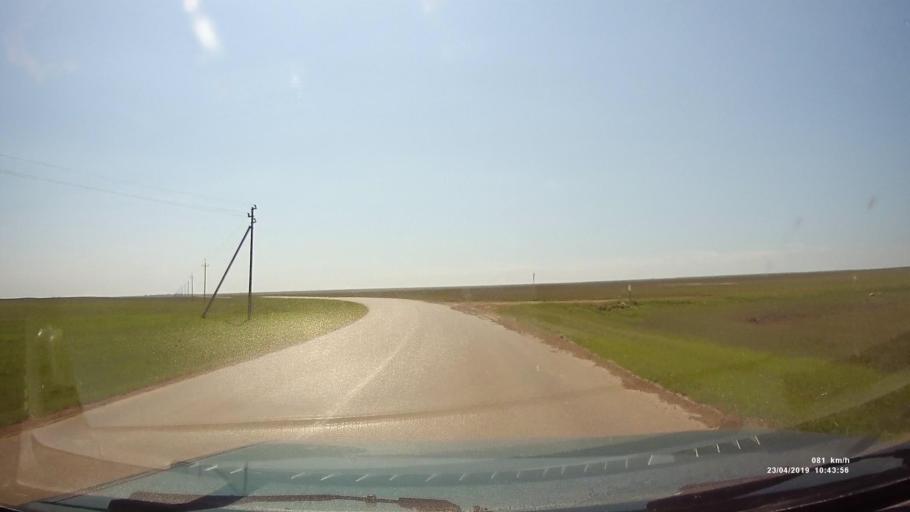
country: RU
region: Kalmykiya
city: Yashalta
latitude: 46.4640
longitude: 42.6506
